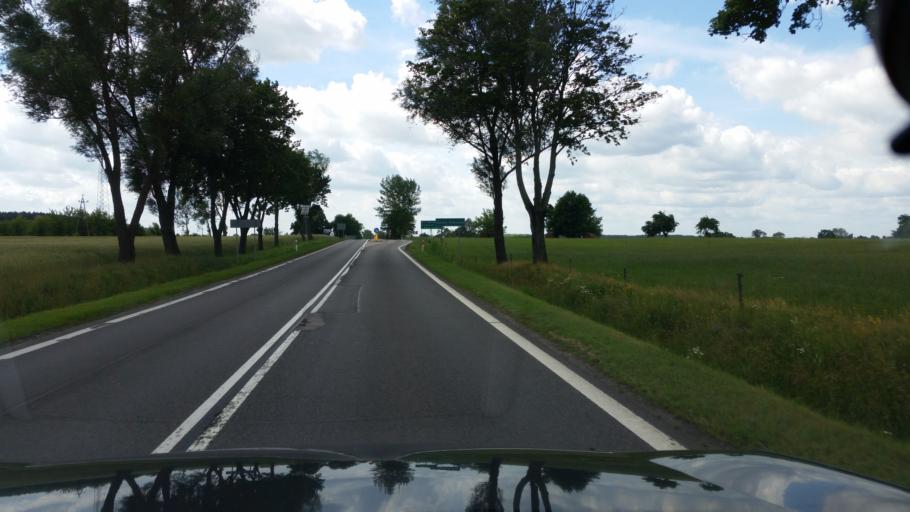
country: PL
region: Podlasie
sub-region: Powiat kolnenski
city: Stawiski
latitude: 53.4680
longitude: 22.2027
